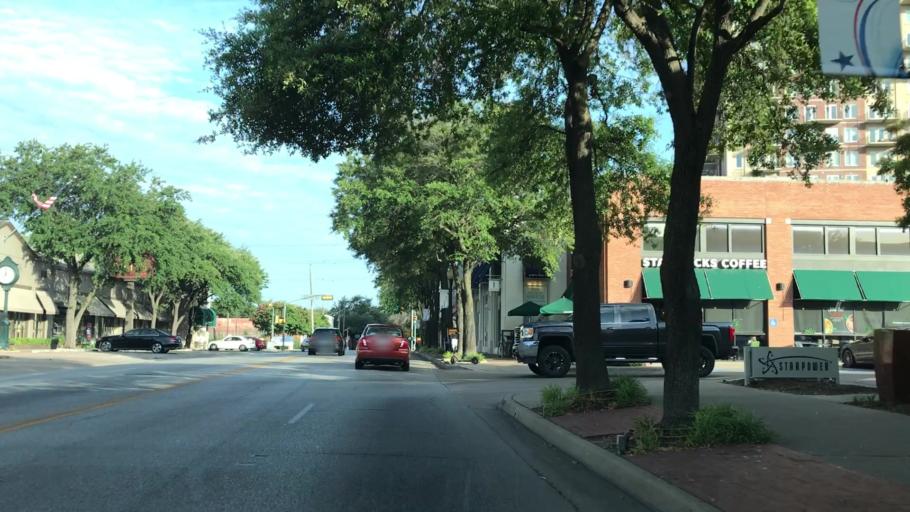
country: US
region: Texas
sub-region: Dallas County
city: Highland Park
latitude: 32.8233
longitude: -96.7892
